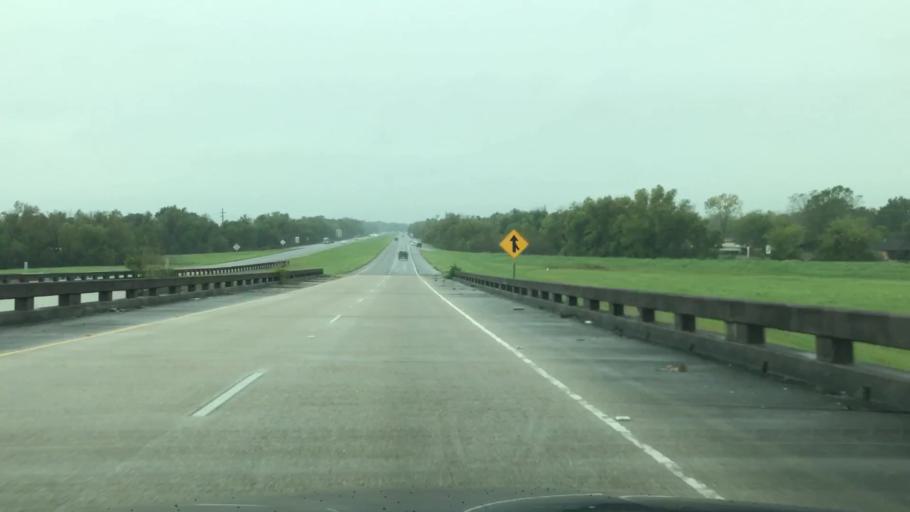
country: US
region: Louisiana
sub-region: Lafourche Parish
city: Raceland
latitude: 29.7061
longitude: -90.5739
